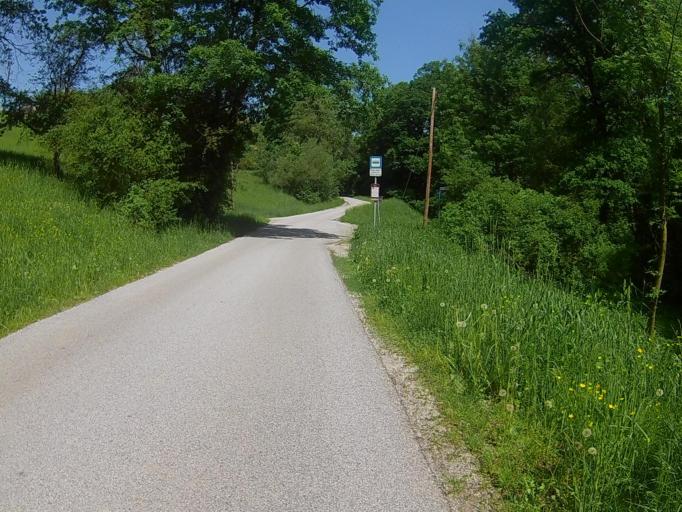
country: SI
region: Duplek
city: Zgornji Duplek
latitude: 46.5619
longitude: 15.7053
